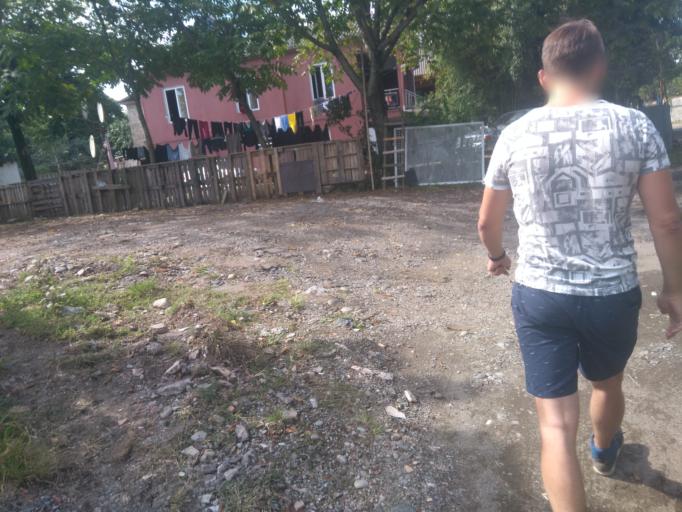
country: GE
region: Ajaria
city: Kobuleti
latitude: 41.8633
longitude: 41.7841
